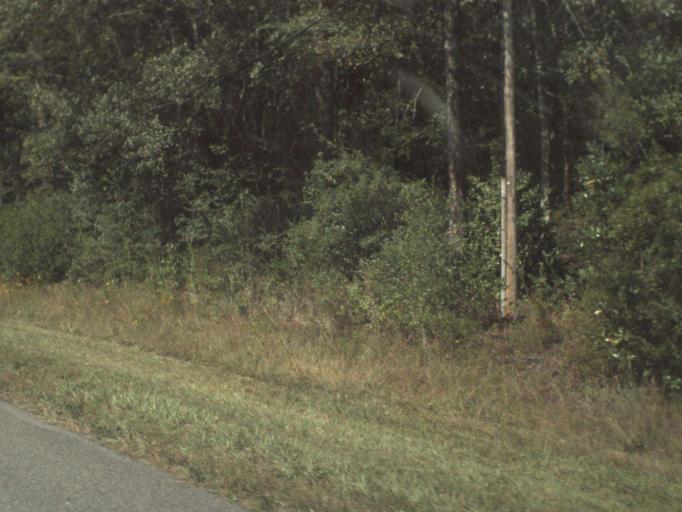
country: US
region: Florida
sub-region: Walton County
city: Freeport
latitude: 30.4736
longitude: -85.9817
